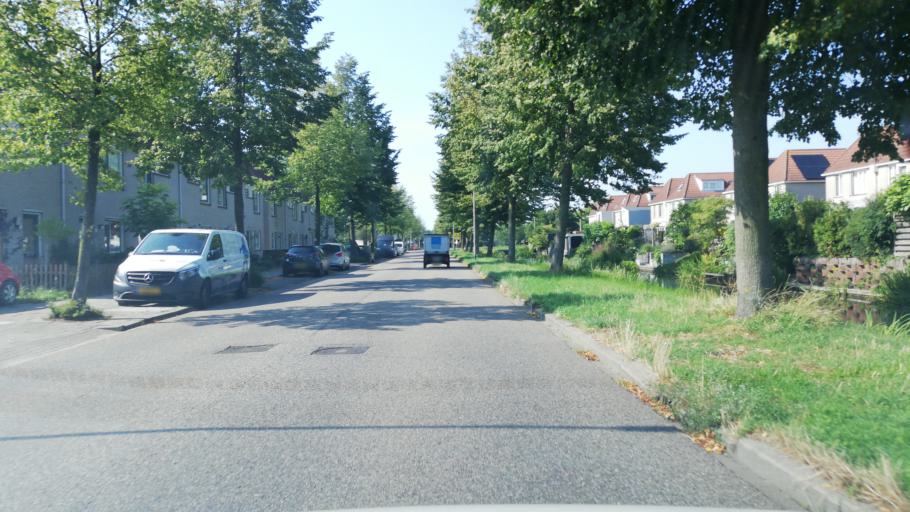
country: NL
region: Overijssel
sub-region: Gemeente Zwolle
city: Zwolle
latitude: 52.4926
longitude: 6.1011
